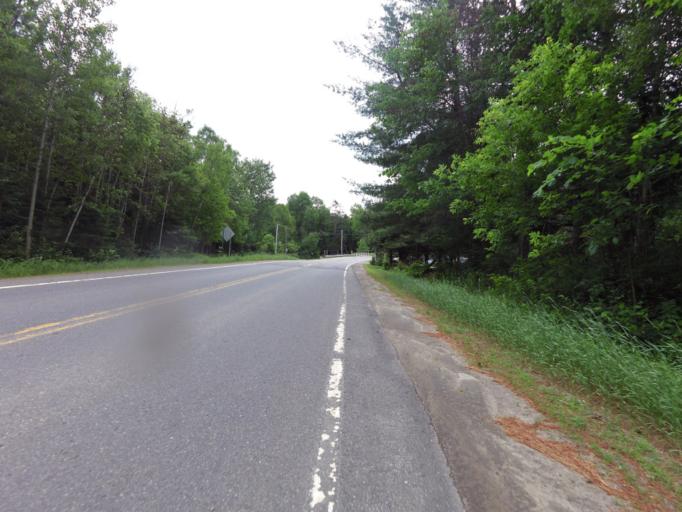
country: CA
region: Quebec
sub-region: Laurentides
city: Brownsburg-Chatham
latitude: 45.8794
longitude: -74.5676
